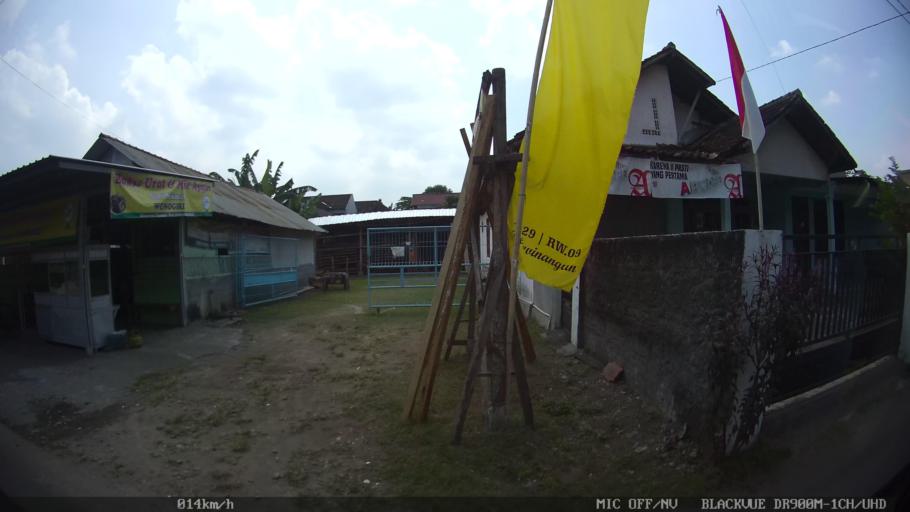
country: ID
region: Daerah Istimewa Yogyakarta
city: Yogyakarta
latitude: -7.8131
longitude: 110.3972
